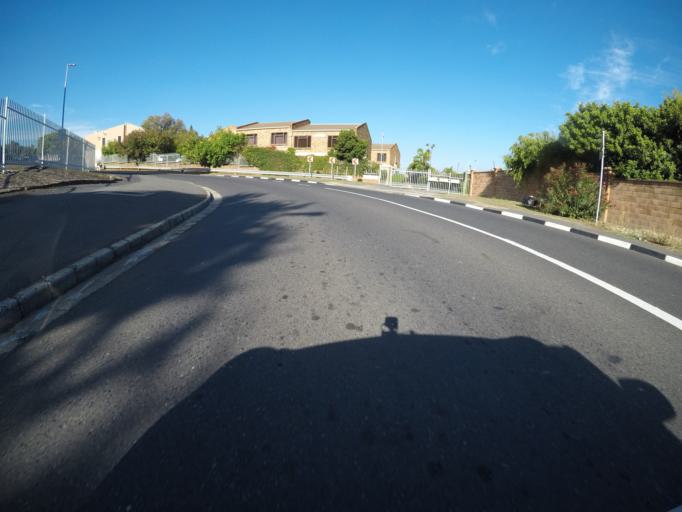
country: ZA
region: Western Cape
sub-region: City of Cape Town
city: Kraaifontein
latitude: -33.8809
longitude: 18.6439
